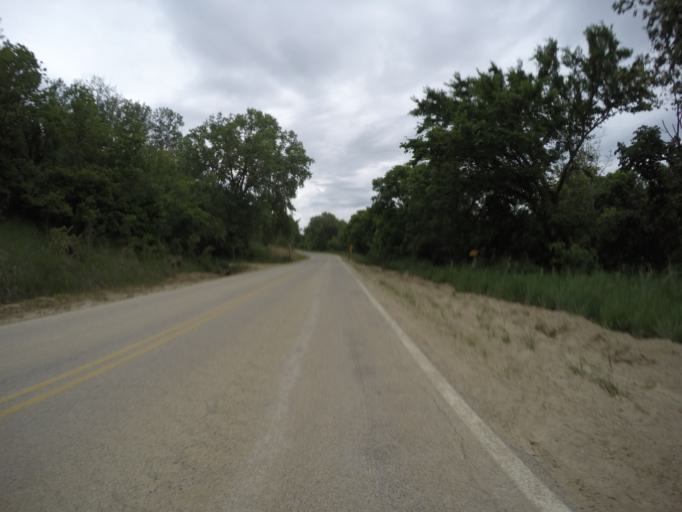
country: US
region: Kansas
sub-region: Pottawatomie County
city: Wamego
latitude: 39.1828
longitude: -96.4025
